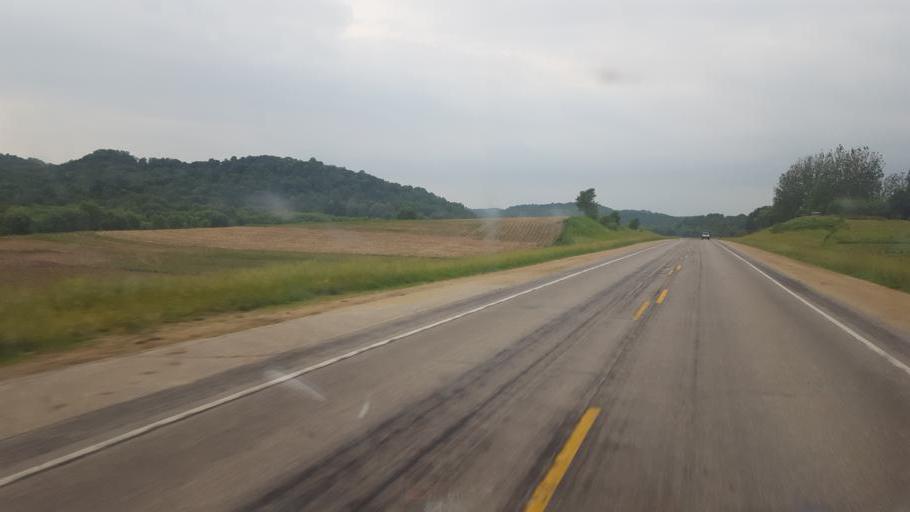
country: US
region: Wisconsin
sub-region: Vernon County
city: Hillsboro
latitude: 43.6601
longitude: -90.3790
